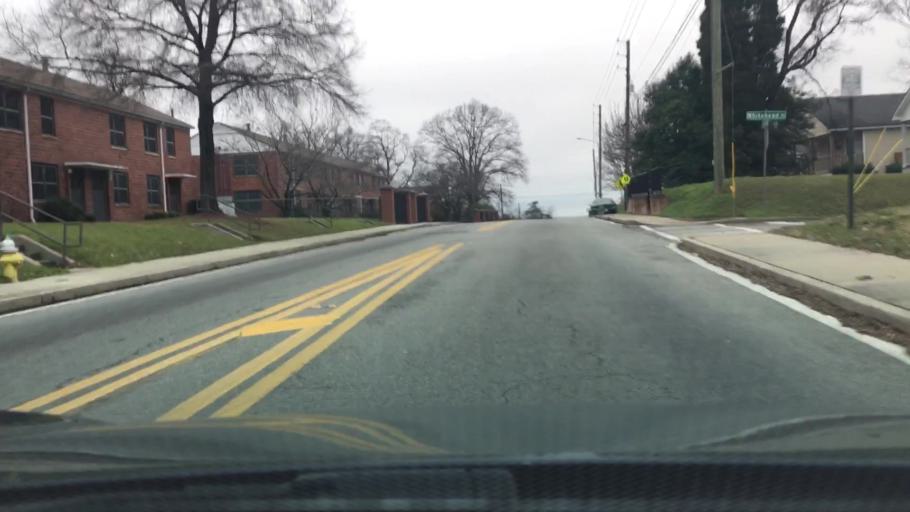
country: US
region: Georgia
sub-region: Bibb County
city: Macon
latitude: 32.8170
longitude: -83.6430
